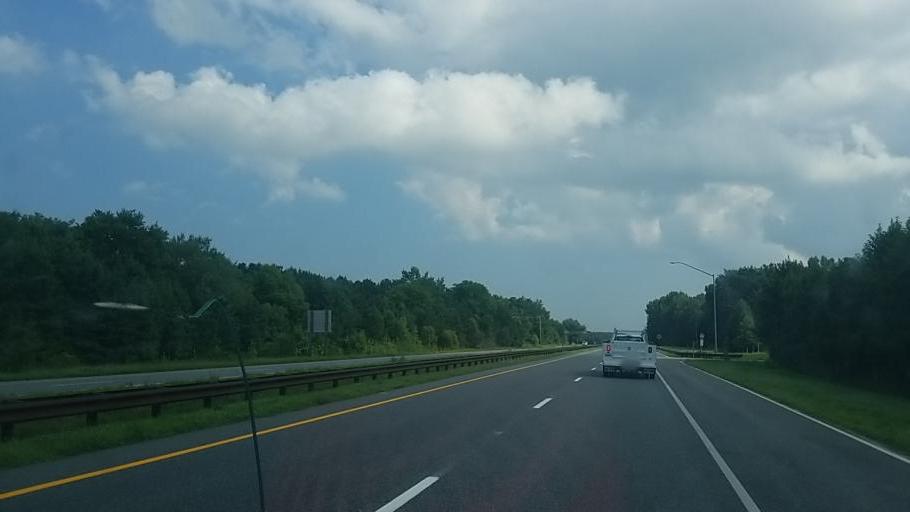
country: US
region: Delaware
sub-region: Sussex County
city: Selbyville
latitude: 38.4381
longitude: -75.2250
